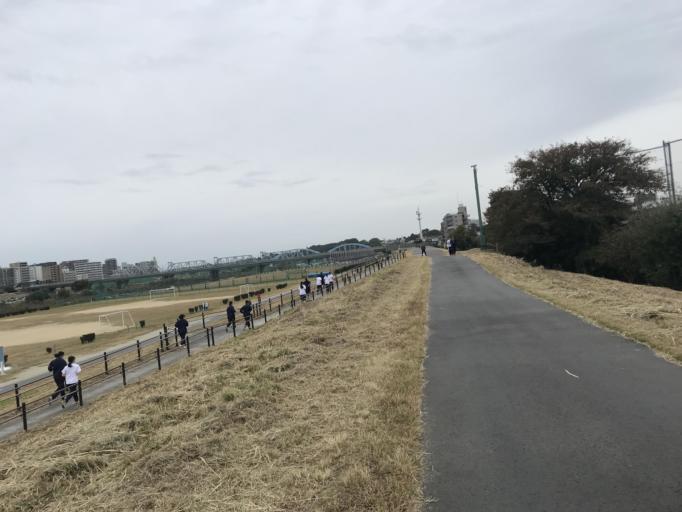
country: JP
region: Kanagawa
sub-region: Kawasaki-shi
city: Kawasaki
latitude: 35.5769
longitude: 139.6744
